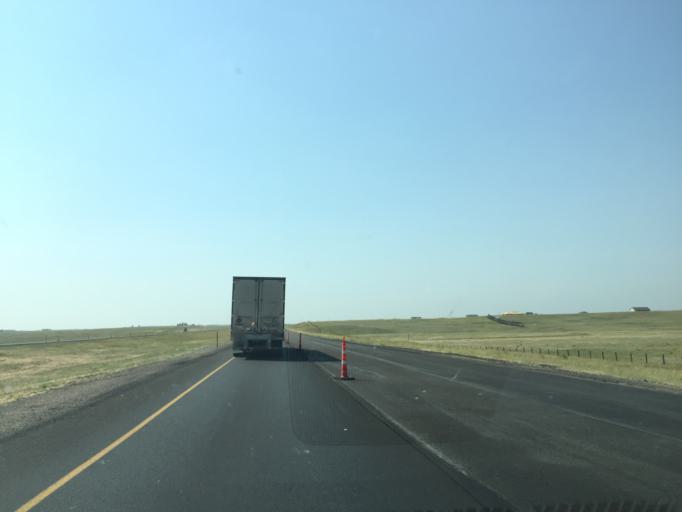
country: US
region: Wyoming
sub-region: Laramie County
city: Ranchettes
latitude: 41.3108
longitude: -104.8577
